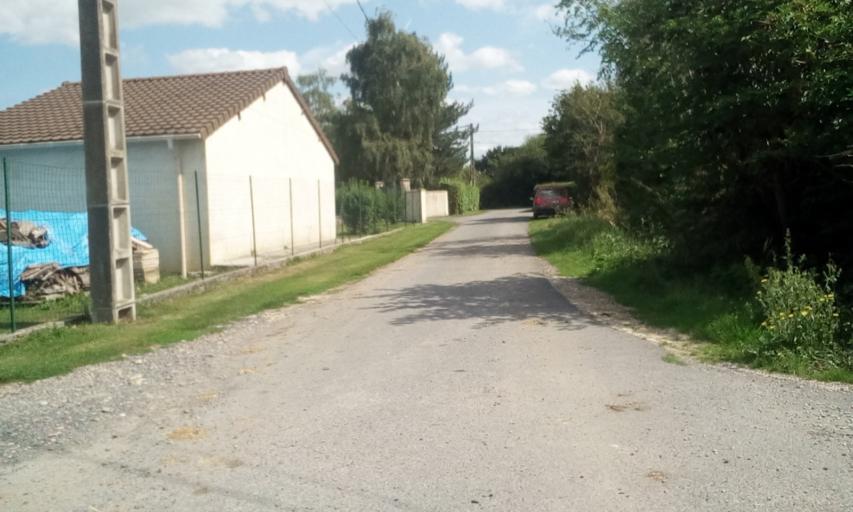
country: FR
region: Lower Normandy
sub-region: Departement du Calvados
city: Argences
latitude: 49.1449
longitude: -0.1487
